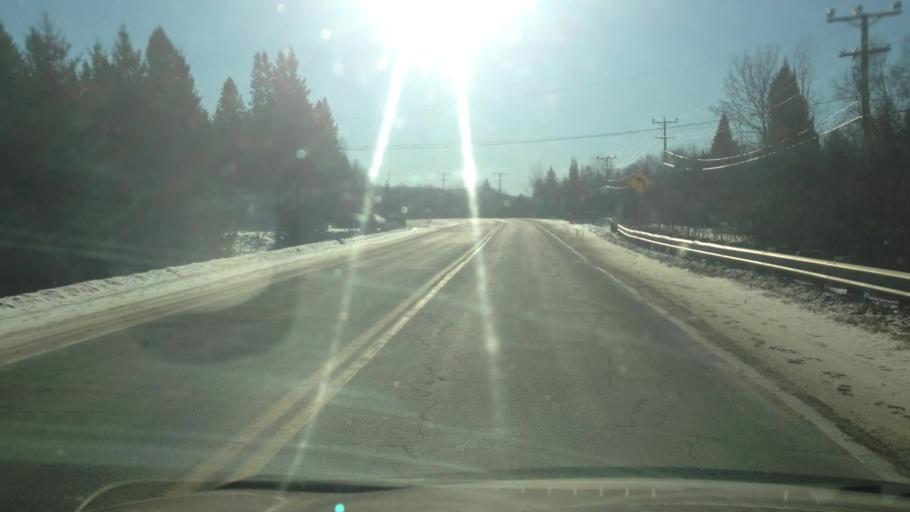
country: CA
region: Quebec
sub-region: Laurentides
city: Mont-Tremblant
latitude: 46.0973
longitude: -74.6062
